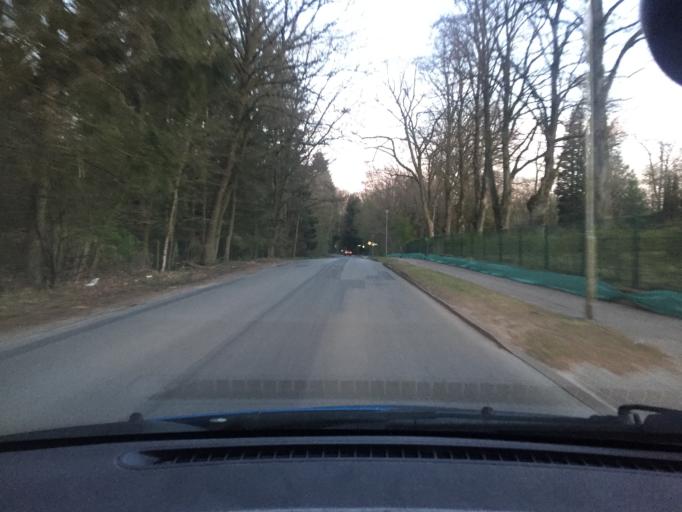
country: DE
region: Lower Saxony
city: Buchholz in der Nordheide
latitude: 53.3039
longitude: 9.8708
